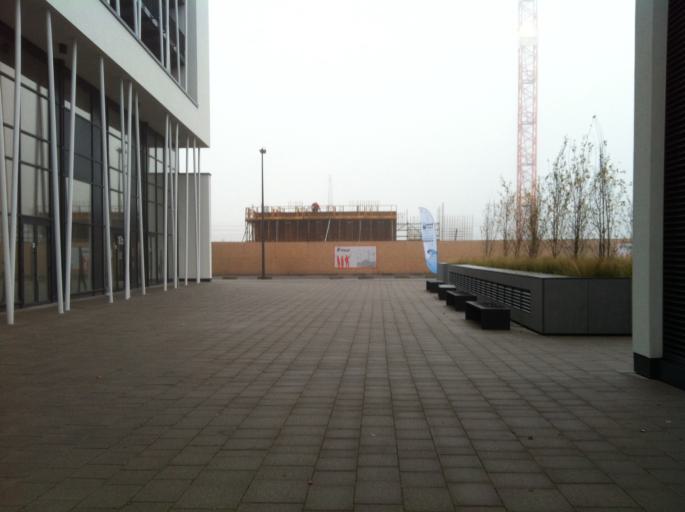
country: LU
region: Luxembourg
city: Belvaux
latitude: 49.5024
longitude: 5.9417
